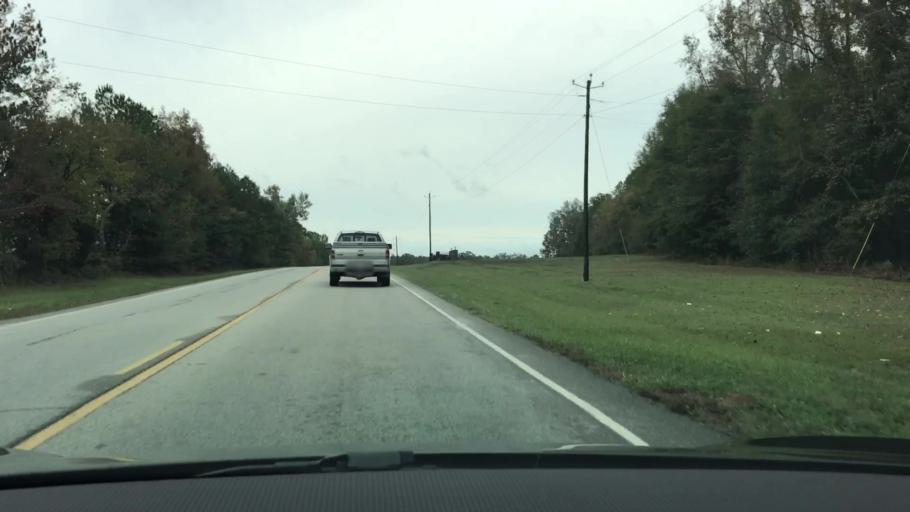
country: US
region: Georgia
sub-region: Warren County
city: Firing Range
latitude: 33.4304
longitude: -82.6857
